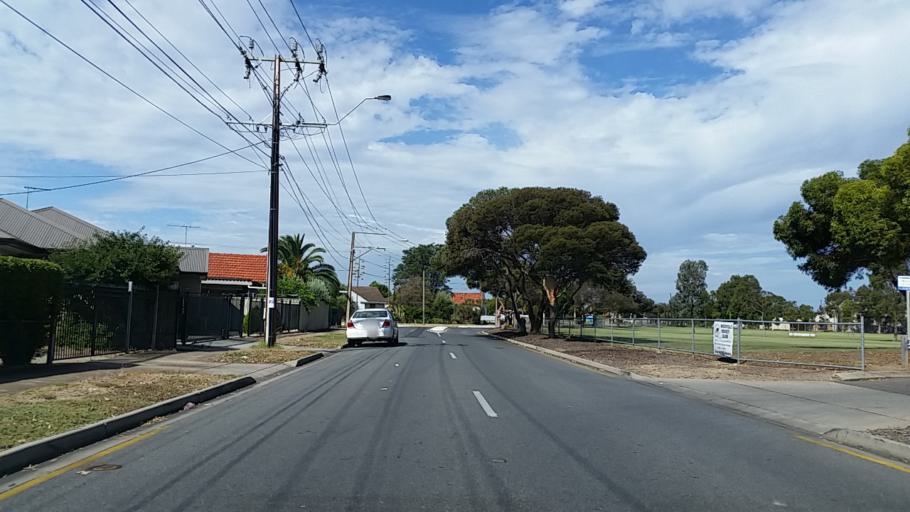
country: AU
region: South Australia
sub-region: Port Adelaide Enfield
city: Alberton
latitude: -34.8604
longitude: 138.5336
